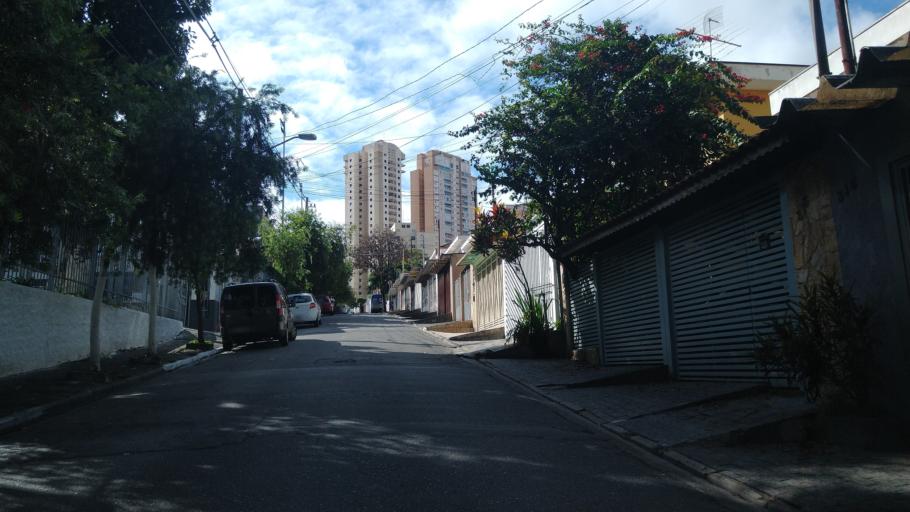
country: BR
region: Sao Paulo
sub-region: Sao Paulo
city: Sao Paulo
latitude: -23.4797
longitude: -46.6433
